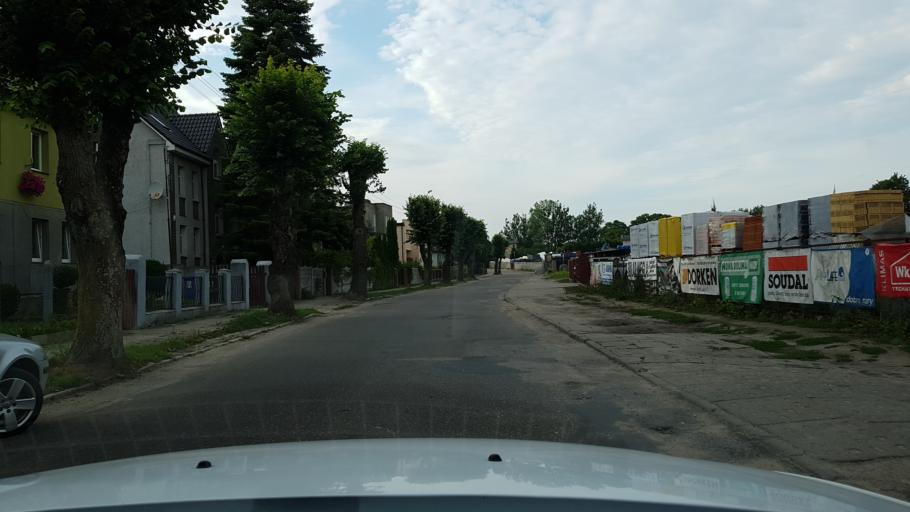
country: PL
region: West Pomeranian Voivodeship
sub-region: Powiat swidwinski
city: Polczyn-Zdroj
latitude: 53.7709
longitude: 16.0941
